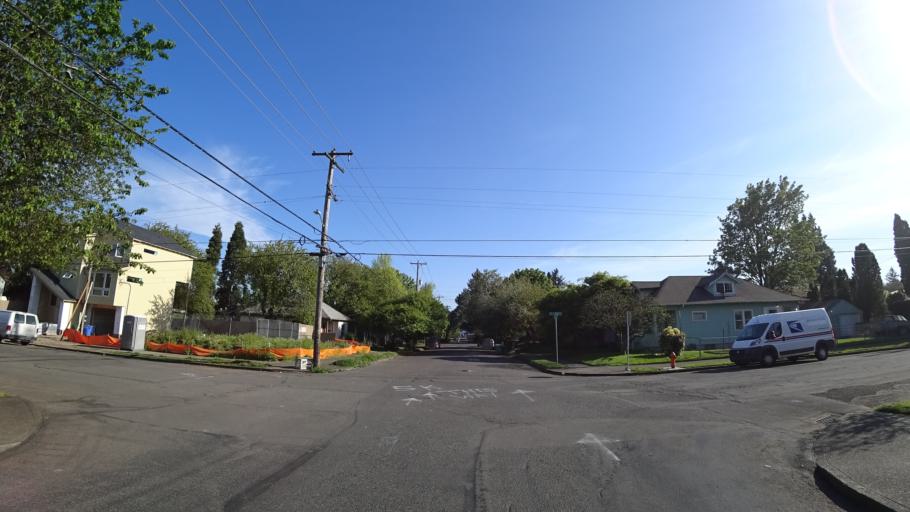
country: US
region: Oregon
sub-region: Clackamas County
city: Milwaukie
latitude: 45.4609
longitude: -122.6451
